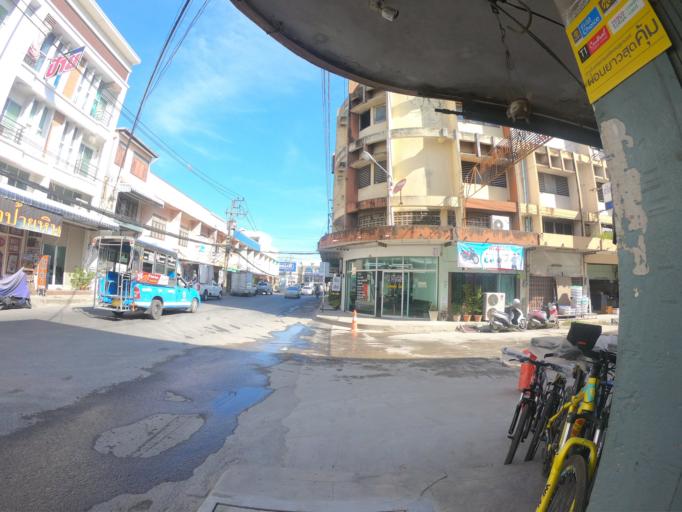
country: TH
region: Nakhon Ratchasima
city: Nakhon Ratchasima
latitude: 14.9787
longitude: 102.0924
